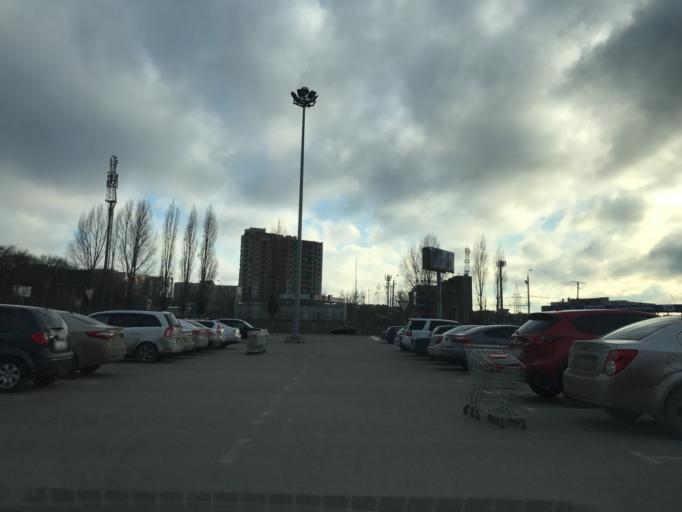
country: RU
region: Rostov
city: Temernik
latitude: 47.2932
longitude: 39.7332
